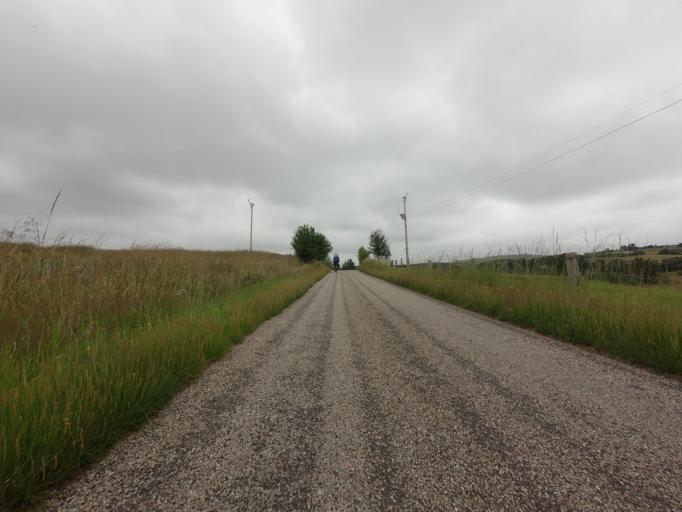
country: GB
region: Scotland
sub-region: Highland
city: Alness
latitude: 58.0061
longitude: -4.4054
